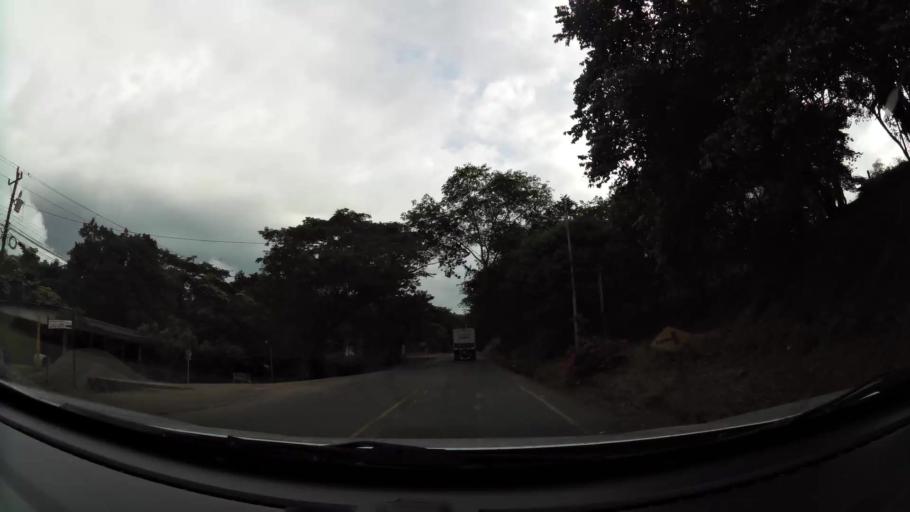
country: CR
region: Guanacaste
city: Juntas
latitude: 10.1611
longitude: -84.9175
